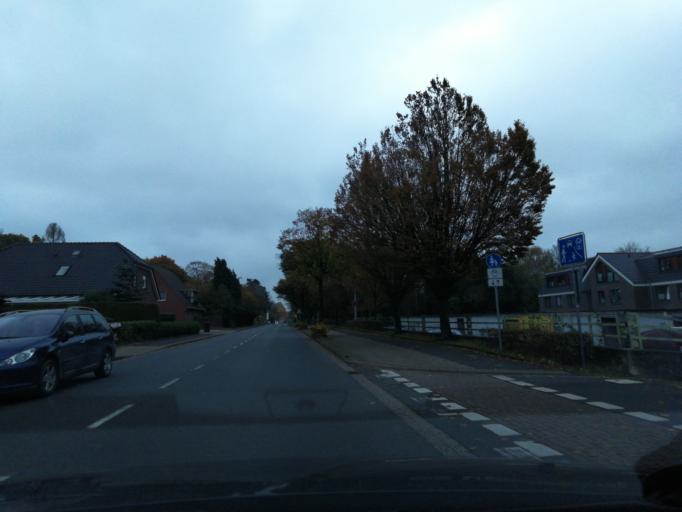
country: DE
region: Lower Saxony
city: Schortens
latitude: 53.5439
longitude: 7.9412
